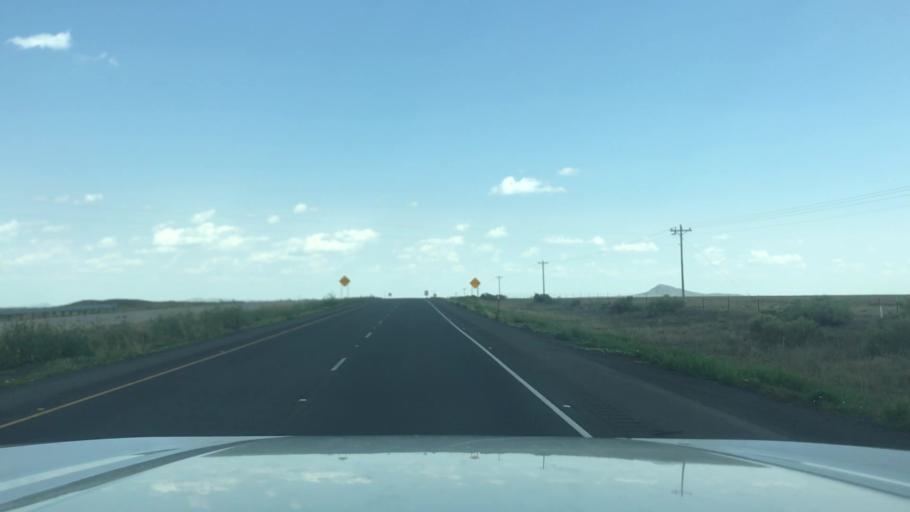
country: US
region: New Mexico
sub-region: Union County
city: Clayton
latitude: 36.6245
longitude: -103.7023
